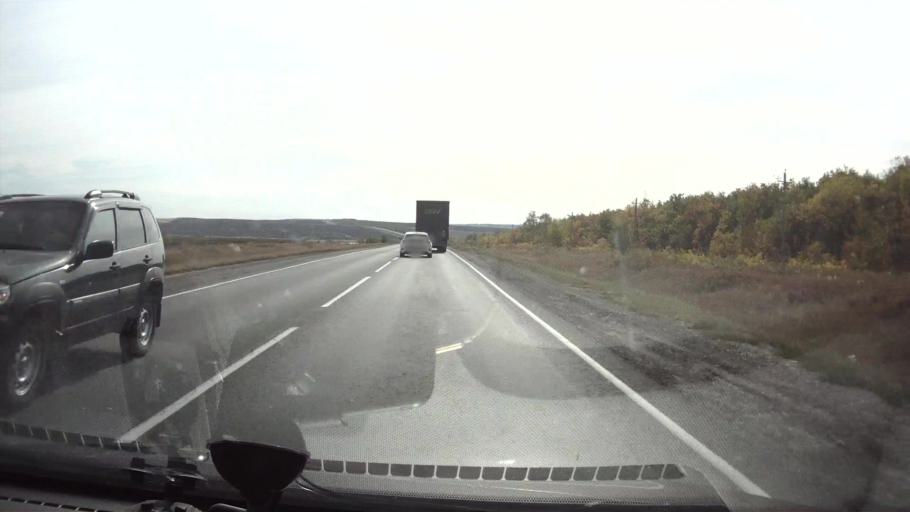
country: RU
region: Saratov
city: Alekseyevka
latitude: 52.2655
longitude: 47.9243
